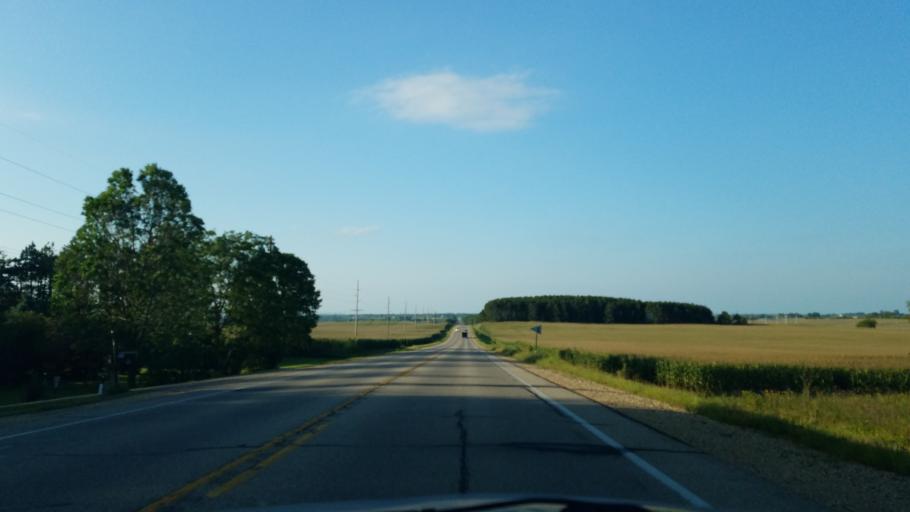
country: US
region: Wisconsin
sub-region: Saint Croix County
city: Roberts
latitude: 45.0279
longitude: -92.5376
